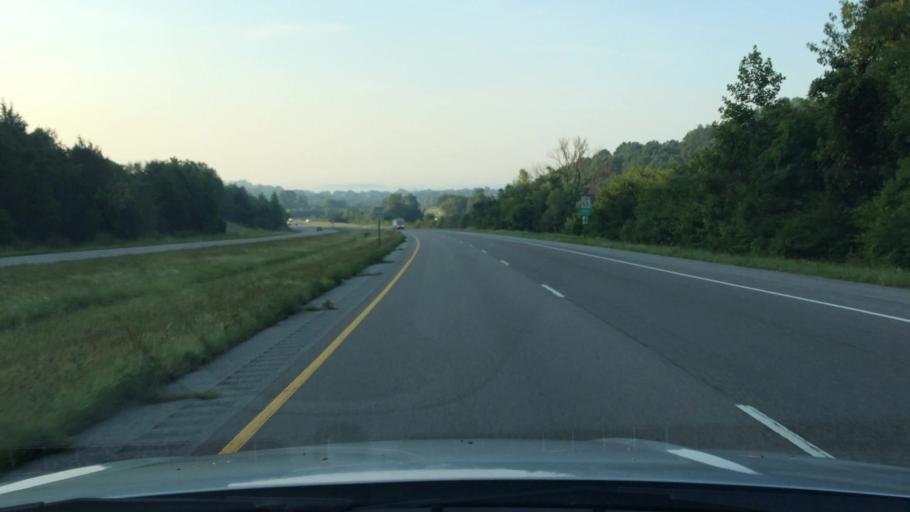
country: US
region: Tennessee
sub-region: Giles County
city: Pulaski
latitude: 35.1761
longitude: -87.0595
